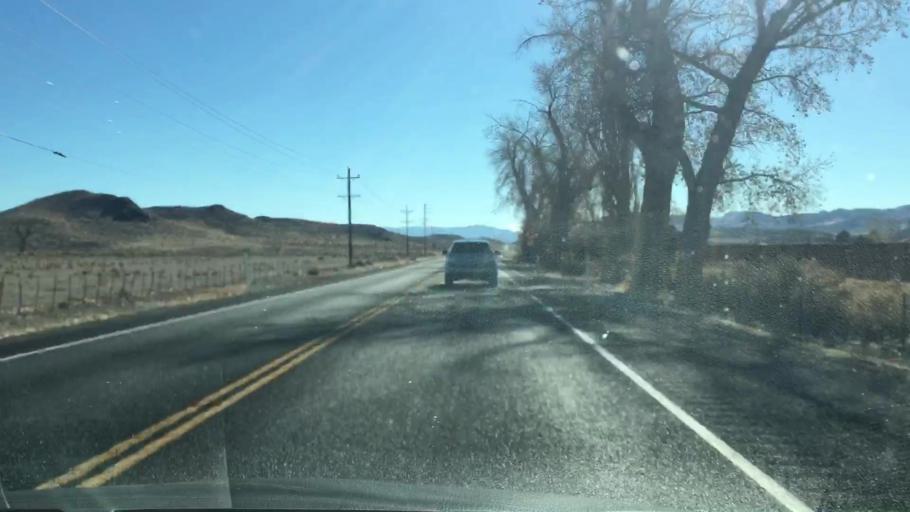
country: US
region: Nevada
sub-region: Lyon County
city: Yerington
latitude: 39.0285
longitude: -119.1816
